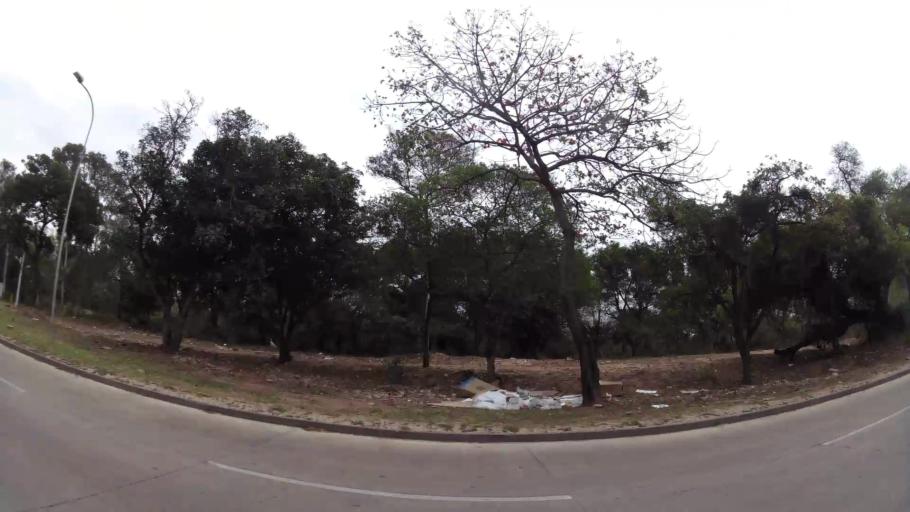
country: BO
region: Santa Cruz
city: Santa Cruz de la Sierra
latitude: -17.7638
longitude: -63.2042
